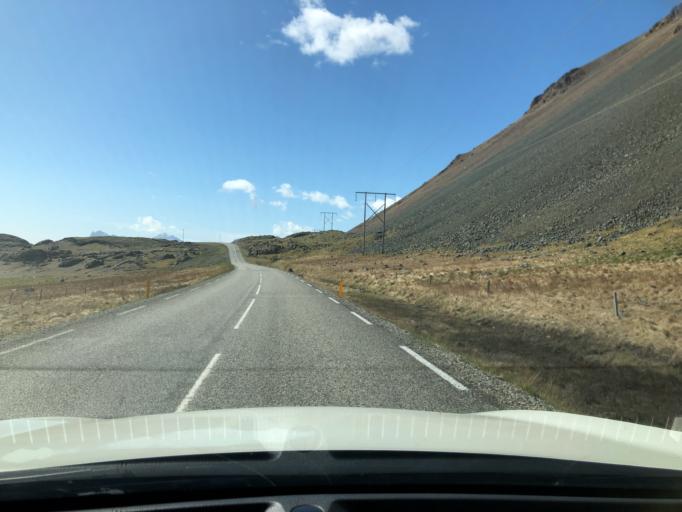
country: IS
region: East
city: Hoefn
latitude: 64.4276
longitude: -14.7094
